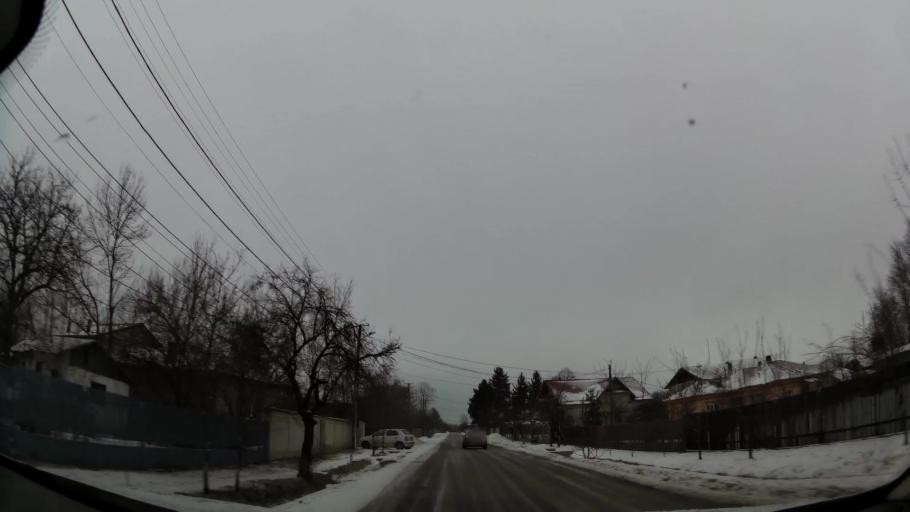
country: RO
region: Prahova
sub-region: Comuna Poenarii-Burchi
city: Ologeni
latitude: 44.7285
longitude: 25.9577
